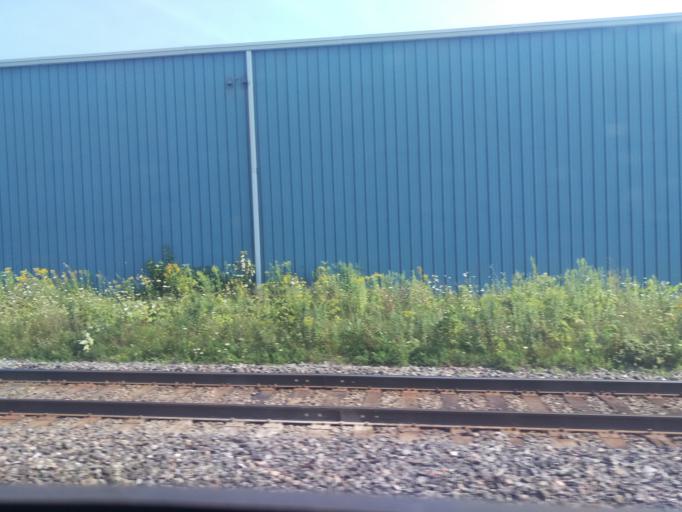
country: CA
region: Ontario
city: Brockville
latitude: 44.5931
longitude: -75.6906
